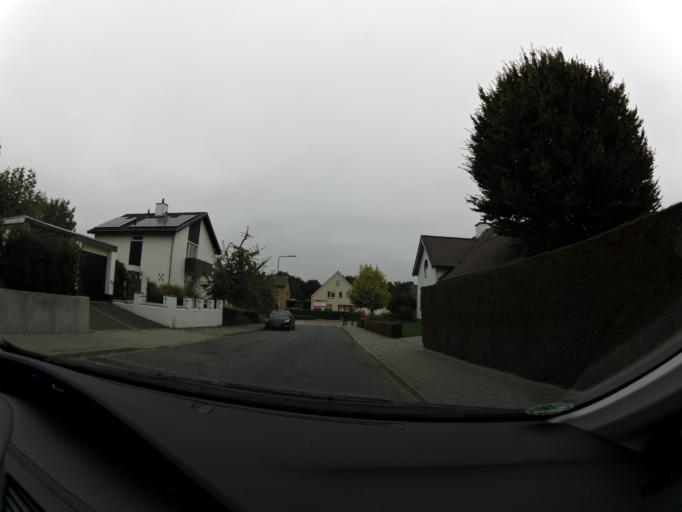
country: NL
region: Limburg
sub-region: Gemeente Heerlen
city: Mariarade
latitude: 50.9347
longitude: 5.9338
